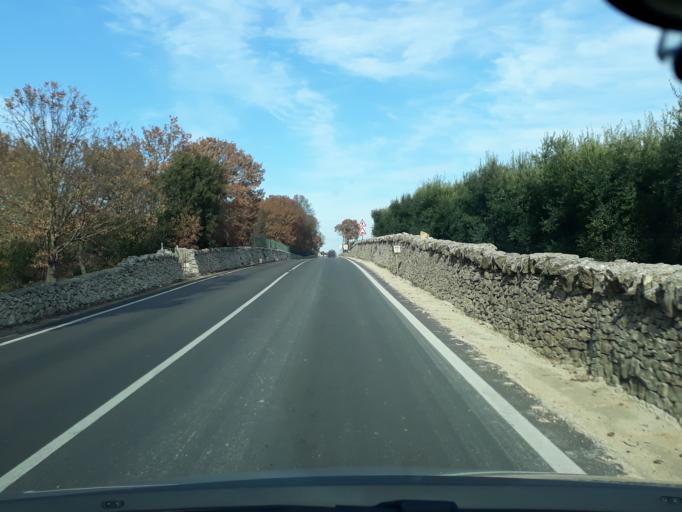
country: IT
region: Apulia
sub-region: Provincia di Bari
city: Locorotondo
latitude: 40.7706
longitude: 17.3340
